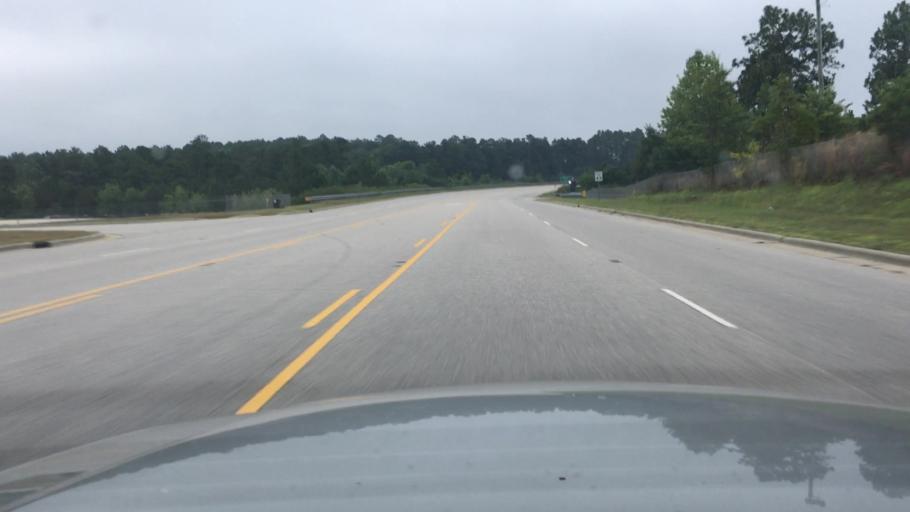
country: US
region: North Carolina
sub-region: Cumberland County
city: Fayetteville
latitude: 35.0174
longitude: -78.8903
